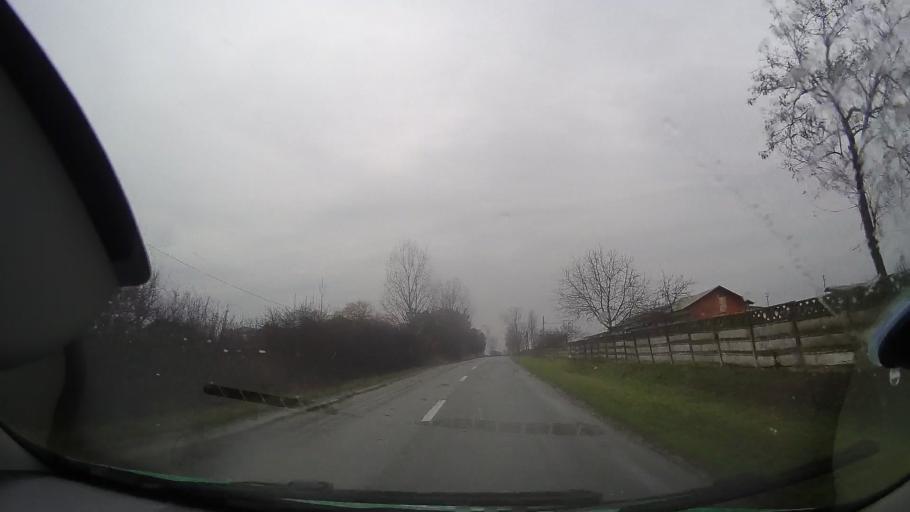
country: RO
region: Bihor
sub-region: Comuna Tinca
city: Tinca
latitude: 46.7710
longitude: 21.9098
